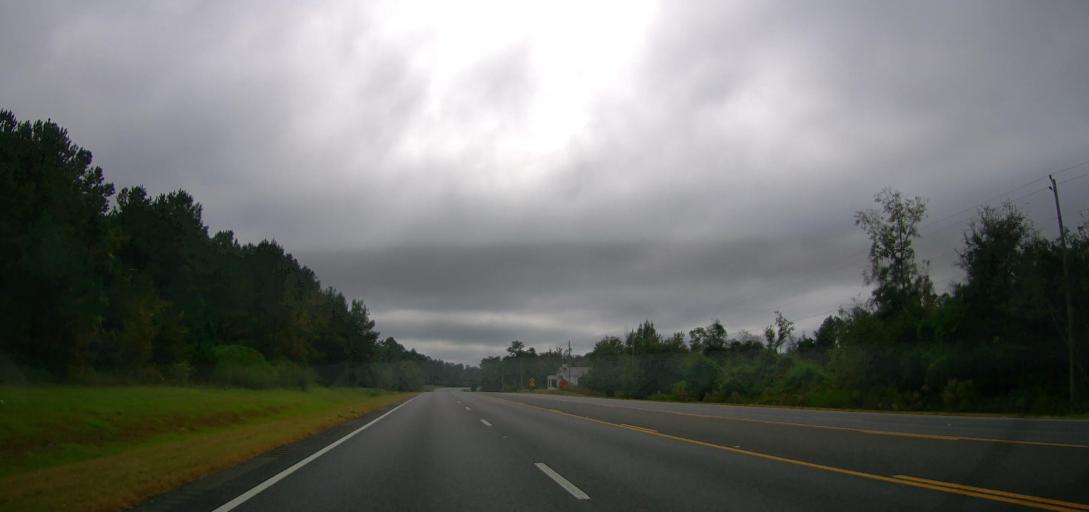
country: US
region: Georgia
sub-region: Thomas County
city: Thomasville
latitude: 30.9274
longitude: -83.9126
